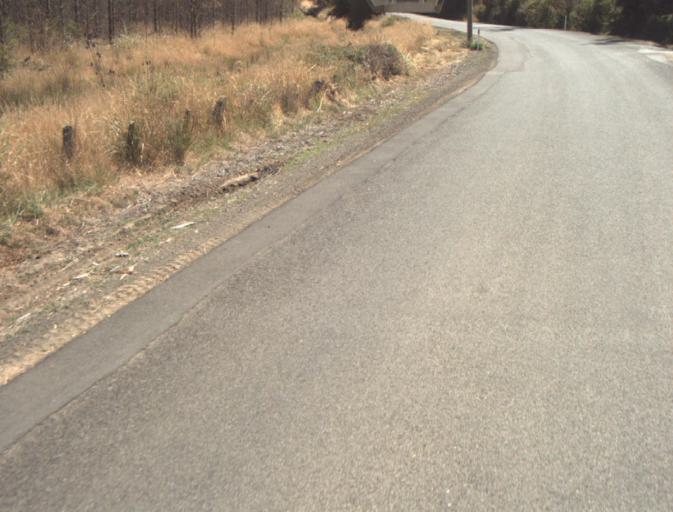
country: AU
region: Tasmania
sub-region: Launceston
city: Newstead
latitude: -41.3829
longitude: 147.2975
